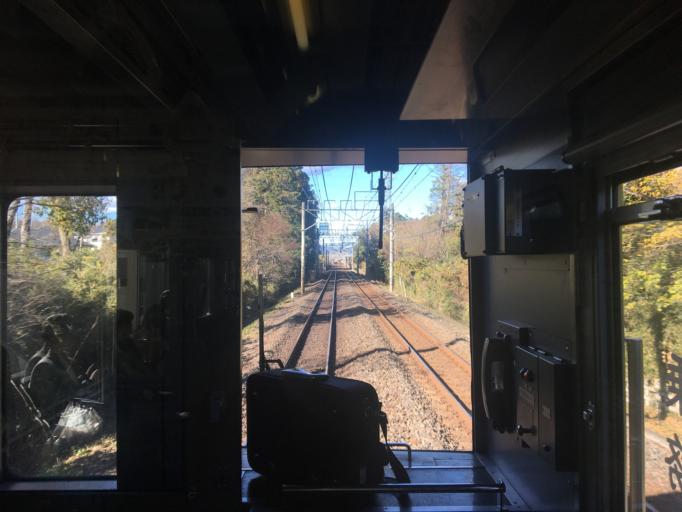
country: JP
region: Saitama
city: Sakado
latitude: 36.0435
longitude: 139.3834
